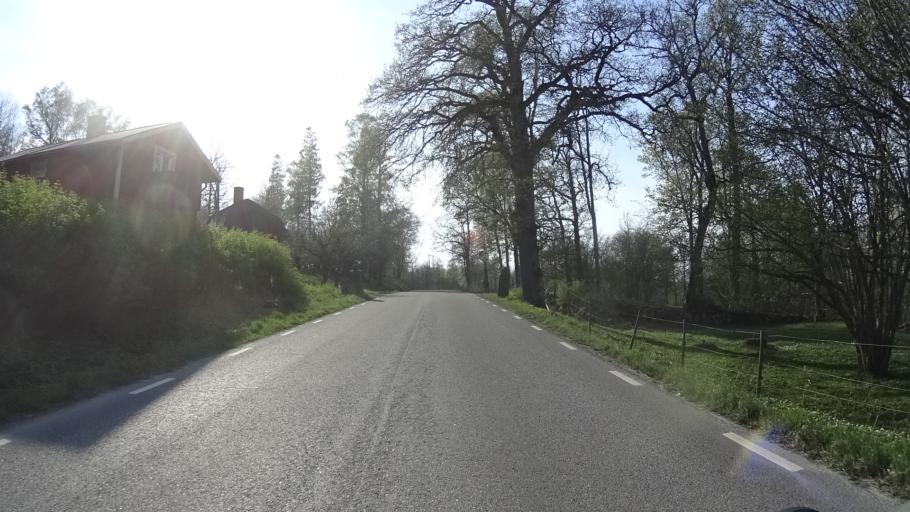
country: SE
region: Vaestra Goetaland
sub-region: Gotene Kommun
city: Goetene
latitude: 58.6226
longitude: 13.4148
